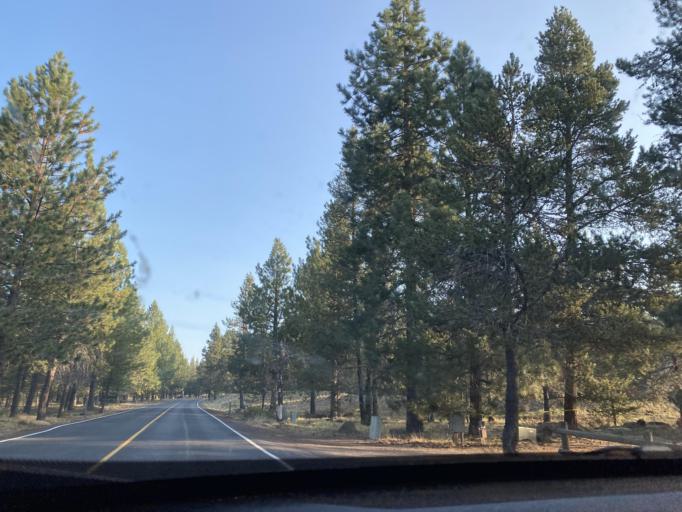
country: US
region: Oregon
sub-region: Deschutes County
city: Sunriver
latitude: 43.8805
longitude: -121.4377
